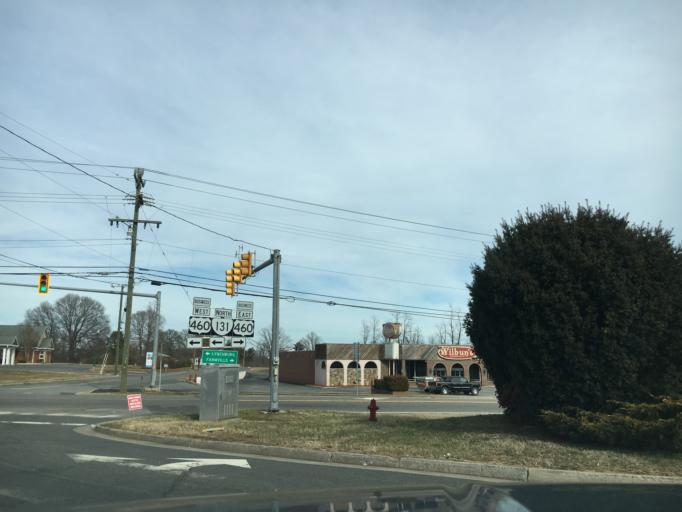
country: US
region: Virginia
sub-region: Appomattox County
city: Appomattox
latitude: 37.3619
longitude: -78.8327
